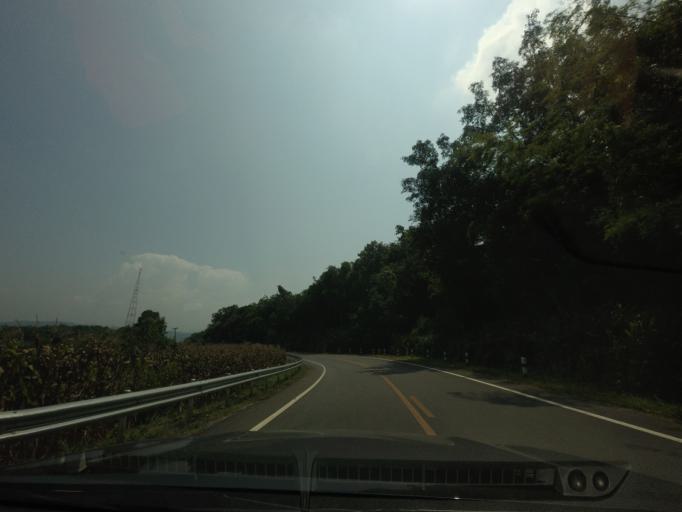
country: TH
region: Nan
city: Santi Suk
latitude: 18.9240
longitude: 100.9133
